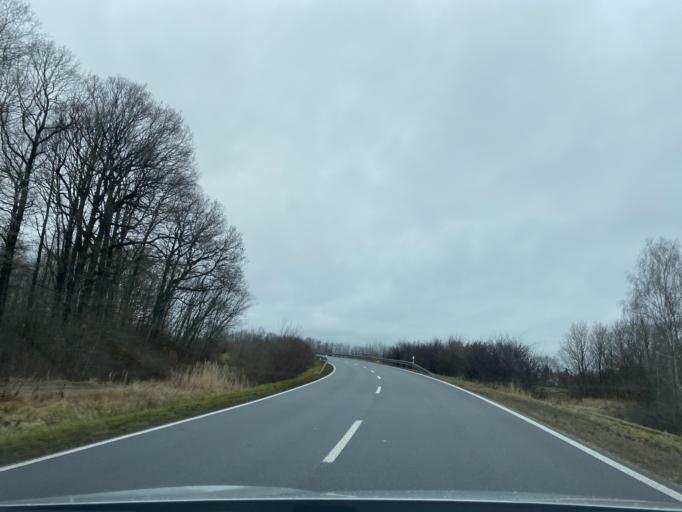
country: DE
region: Saxony
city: Kodersdorf
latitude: 51.2201
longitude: 14.9535
